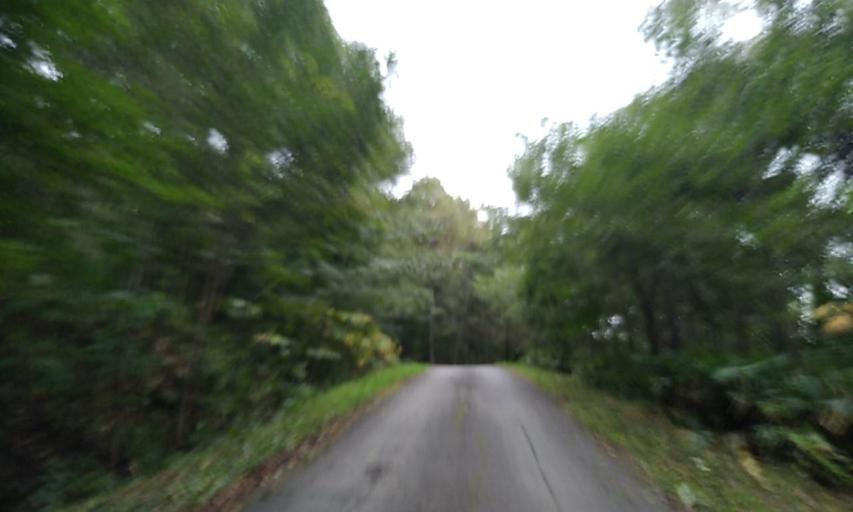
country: JP
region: Hokkaido
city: Obihiro
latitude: 42.8264
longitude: 142.9855
